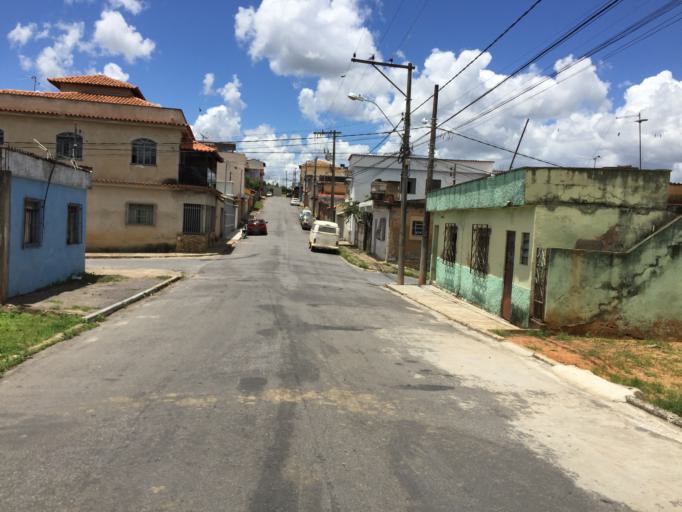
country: BR
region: Minas Gerais
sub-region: Sao Joao Del Rei
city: Sao Joao del Rei
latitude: -21.1436
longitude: -44.2670
